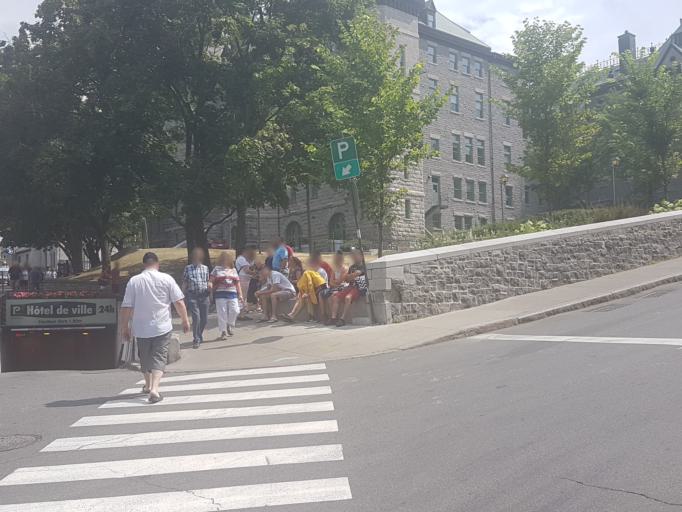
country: CA
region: Quebec
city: Quebec
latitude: 46.8145
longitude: -71.2088
